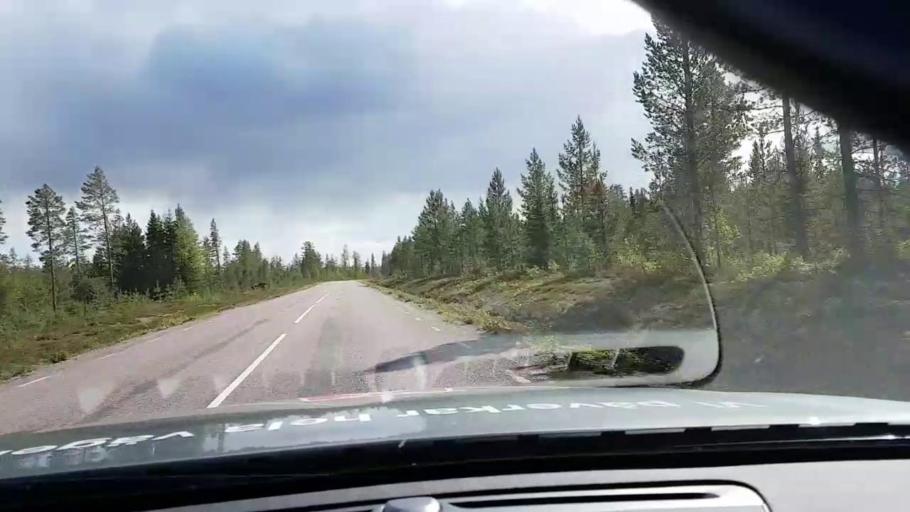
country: SE
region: Vaesterbotten
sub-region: Asele Kommun
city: Asele
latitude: 63.8980
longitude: 17.3494
